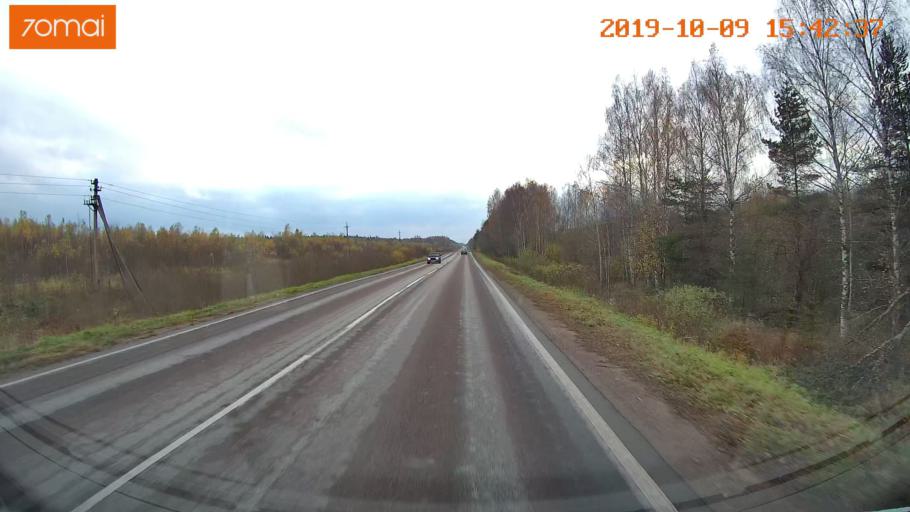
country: RU
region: Kostroma
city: Oktyabr'skiy
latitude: 57.8664
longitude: 41.1035
